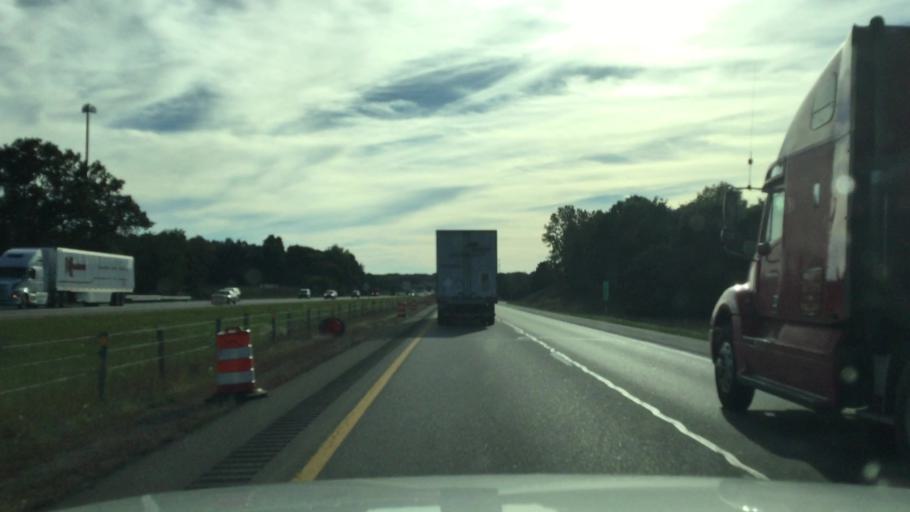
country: US
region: Michigan
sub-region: Calhoun County
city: Battle Creek
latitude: 42.2731
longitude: -85.1705
